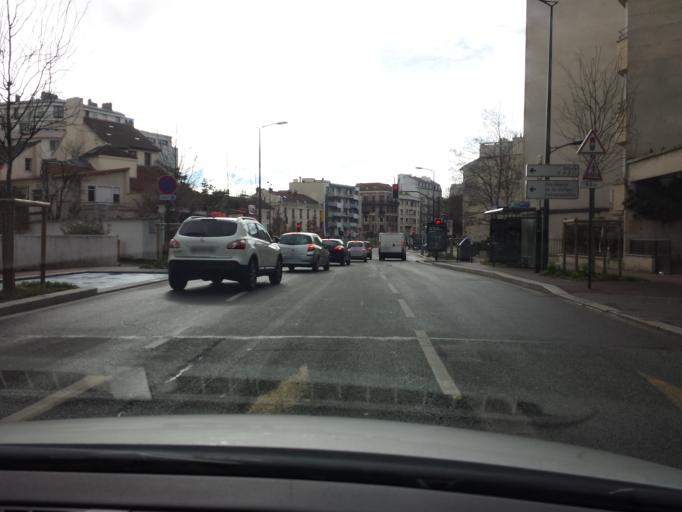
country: FR
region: Ile-de-France
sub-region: Departement des Hauts-de-Seine
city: Bourg-la-Reine
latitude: 48.7775
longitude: 2.3135
